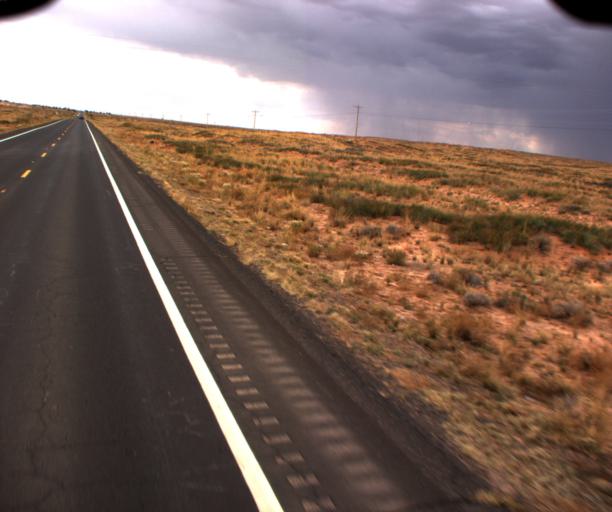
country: US
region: Arizona
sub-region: Coconino County
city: Tuba City
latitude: 36.2610
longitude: -111.0188
